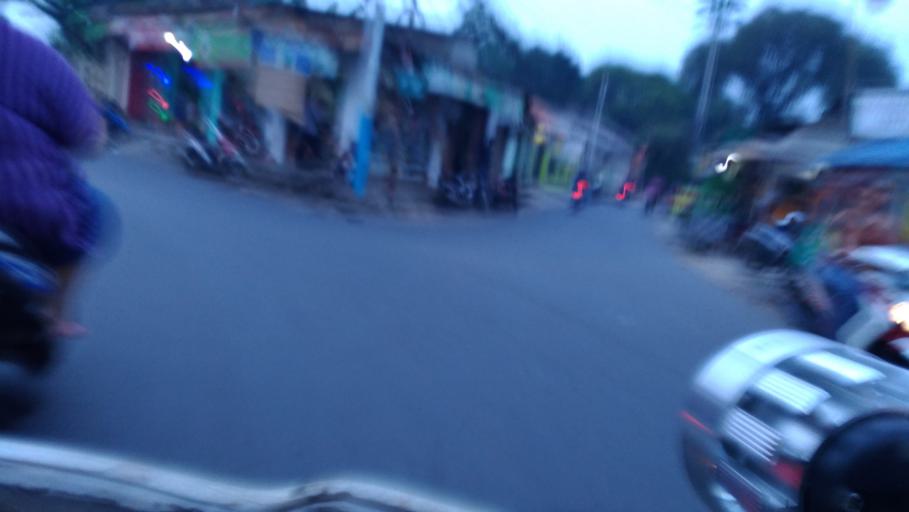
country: ID
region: West Java
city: Depok
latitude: -6.3562
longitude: 106.8796
